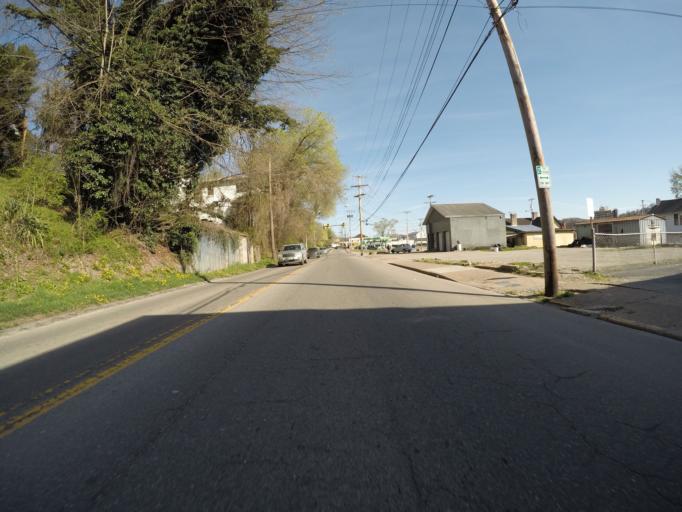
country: US
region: West Virginia
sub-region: Kanawha County
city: Charleston
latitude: 38.3687
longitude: -81.6546
